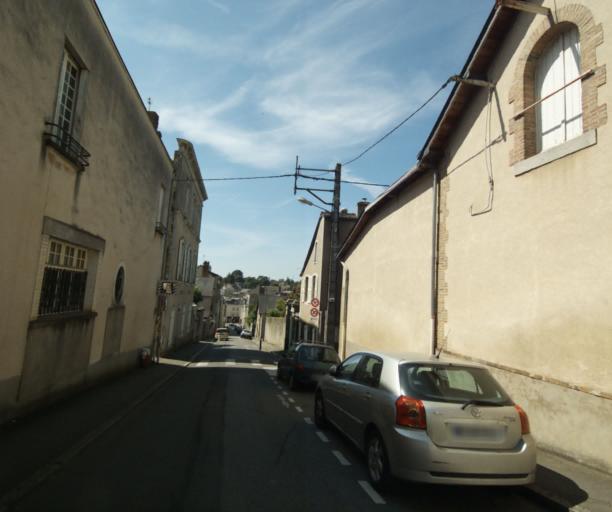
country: FR
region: Pays de la Loire
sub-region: Departement de la Mayenne
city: Laval
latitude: 48.0726
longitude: -0.7764
